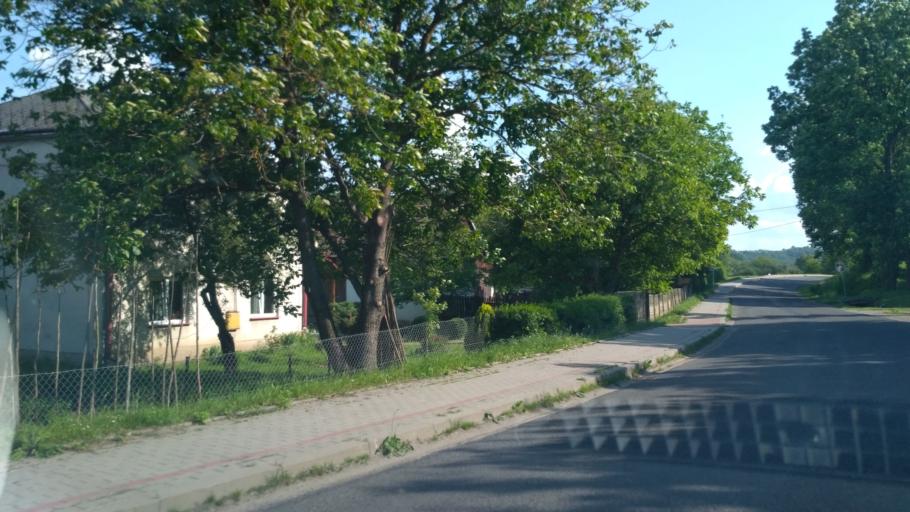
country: PL
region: Subcarpathian Voivodeship
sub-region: Powiat jaroslawski
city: Pruchnik
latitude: 49.8942
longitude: 22.4999
